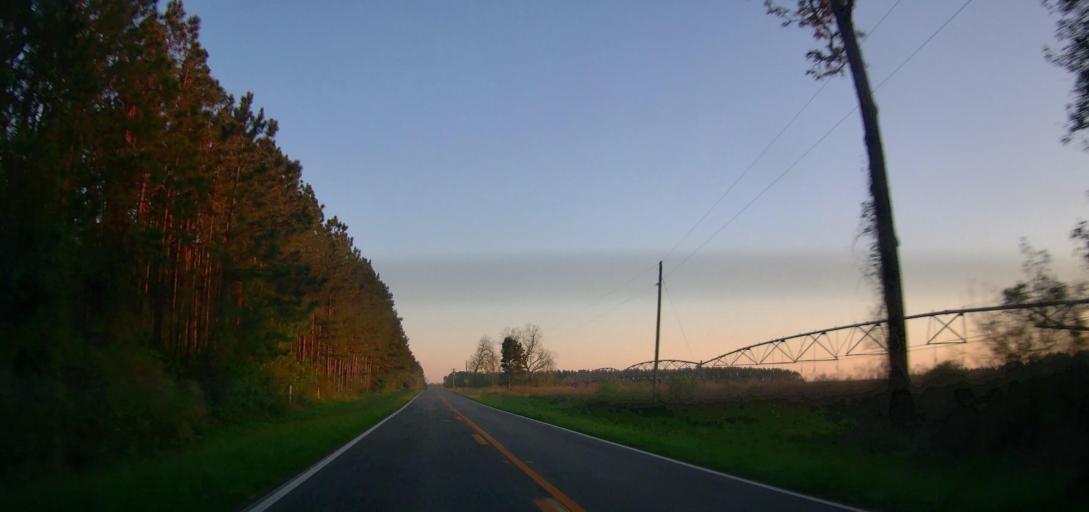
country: US
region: Georgia
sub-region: Ben Hill County
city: Fitzgerald
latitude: 31.7763
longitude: -83.3845
